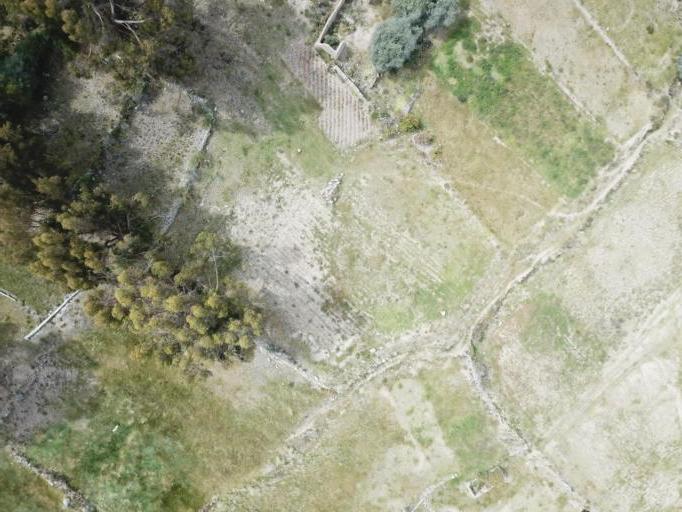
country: BO
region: La Paz
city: Achacachi
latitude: -16.0509
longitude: -68.8132
